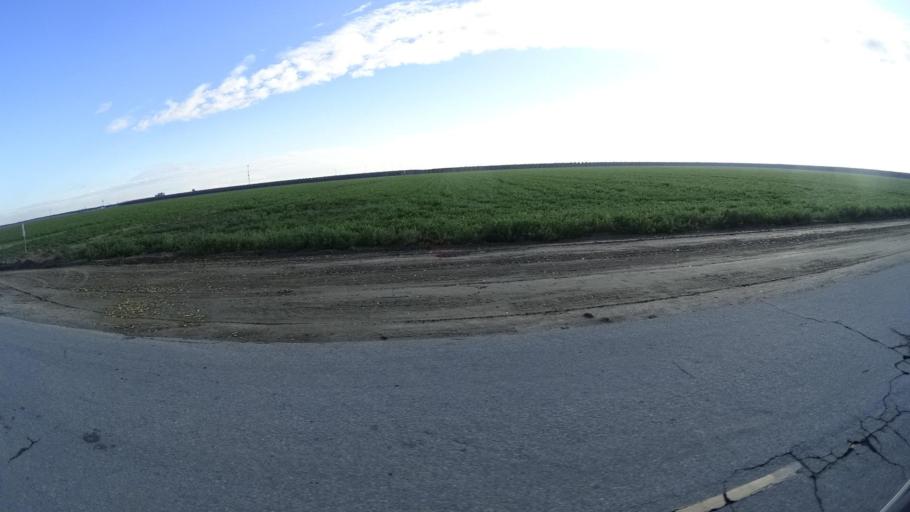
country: US
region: California
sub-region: Kern County
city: Delano
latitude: 35.7466
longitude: -119.3300
